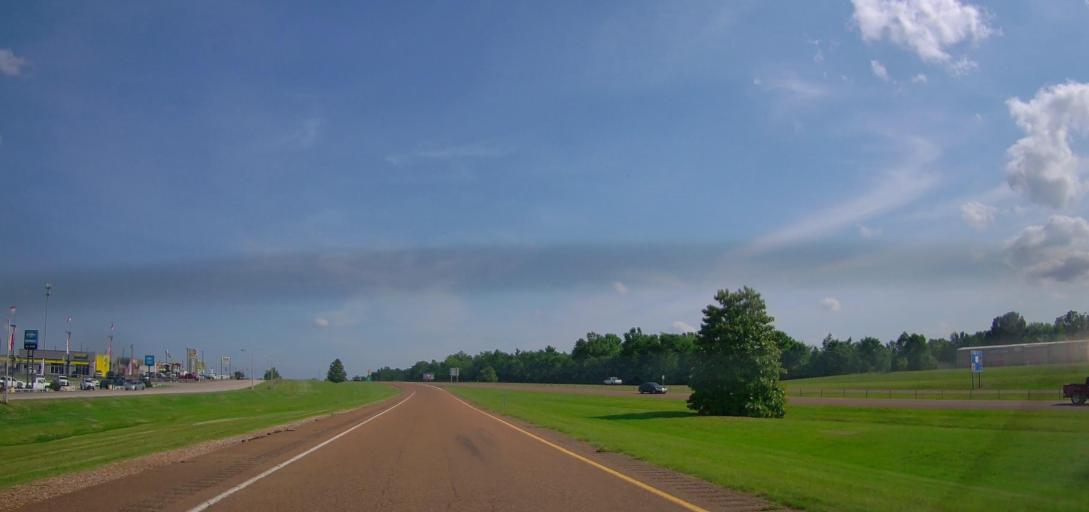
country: US
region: Mississippi
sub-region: De Soto County
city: Olive Branch
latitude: 34.9757
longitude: -89.8632
